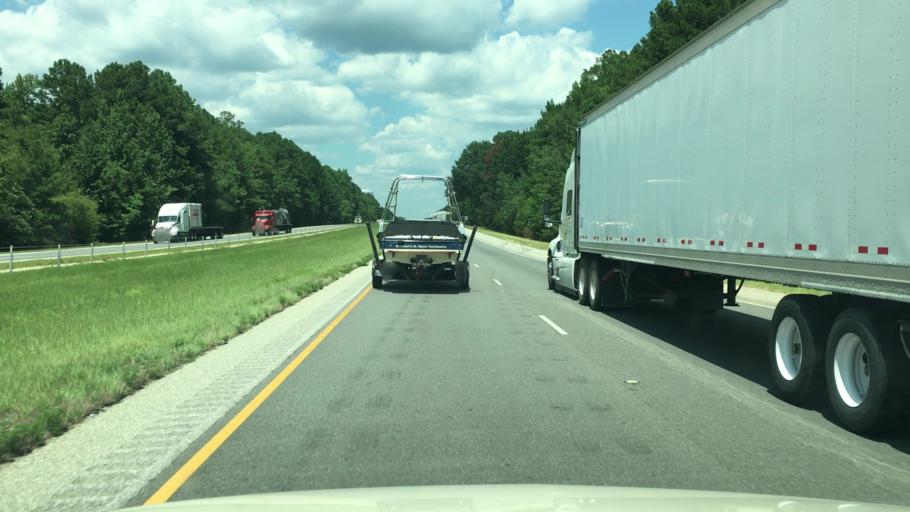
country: US
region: Arkansas
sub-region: Clark County
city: Arkadelphia
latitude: 34.1249
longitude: -93.0893
